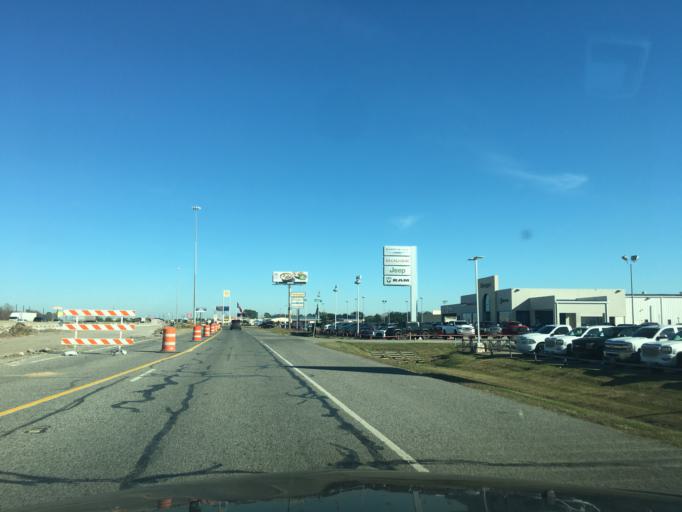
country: US
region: Texas
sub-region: Fort Bend County
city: Rosenberg
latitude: 29.5324
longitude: -95.7843
